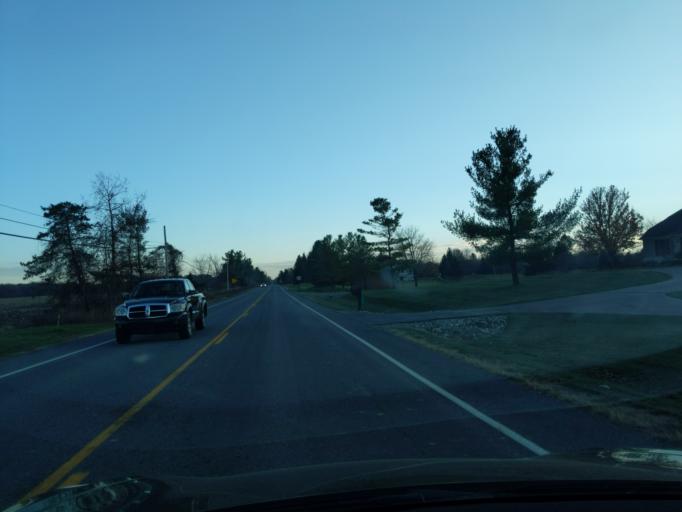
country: US
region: Michigan
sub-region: Ingham County
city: Williamston
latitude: 42.7136
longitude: -84.3149
